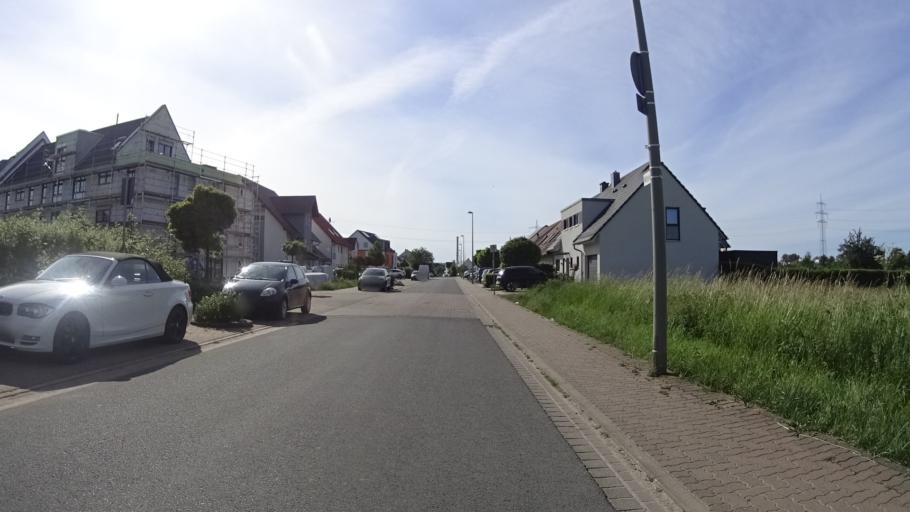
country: DE
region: Bavaria
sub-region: Regierungsbezirk Unterfranken
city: Stockstadt am Main
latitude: 49.9811
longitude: 9.0727
